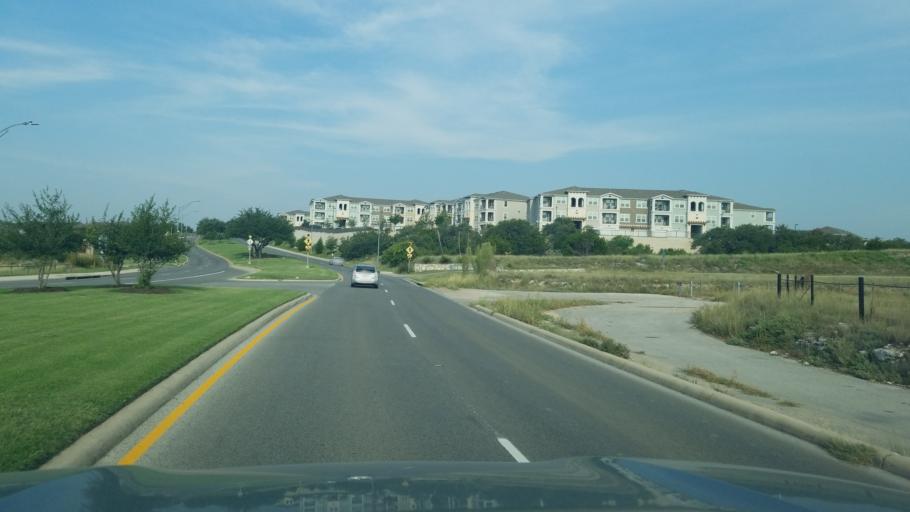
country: US
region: Texas
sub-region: Bexar County
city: Hollywood Park
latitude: 29.6459
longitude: -98.4681
